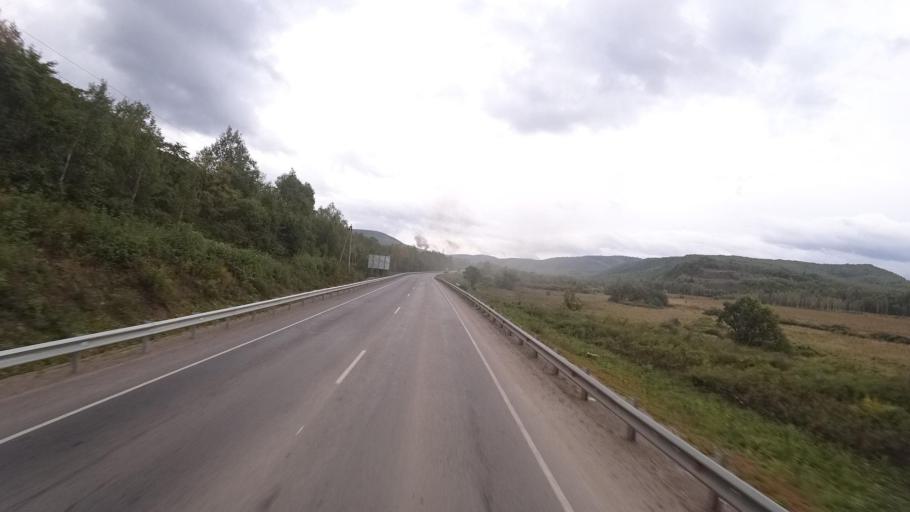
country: RU
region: Jewish Autonomous Oblast
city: Khingansk
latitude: 48.9910
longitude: 131.1181
